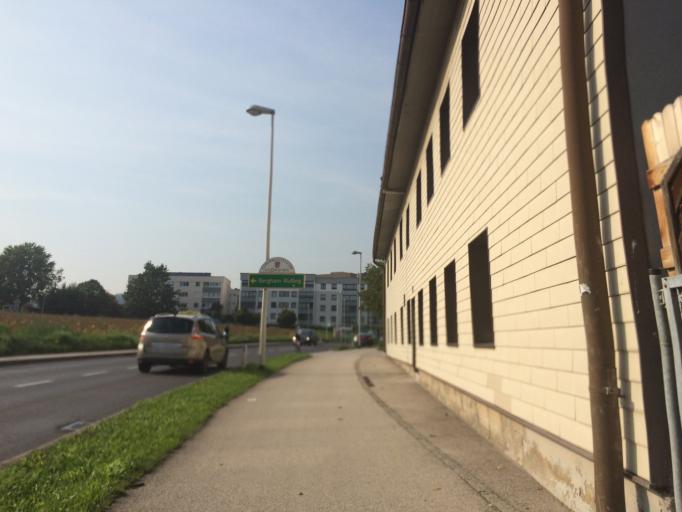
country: AT
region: Upper Austria
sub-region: Politischer Bezirk Linz-Land
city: Leonding
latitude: 48.2777
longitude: 14.2465
